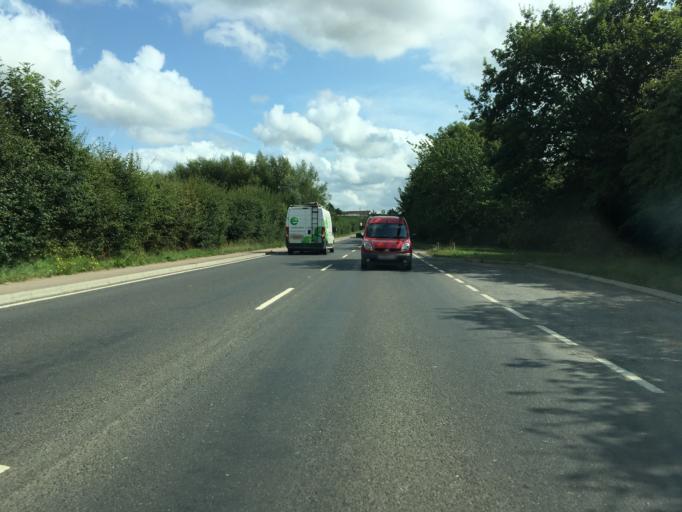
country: GB
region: England
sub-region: Kent
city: Headcorn
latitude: 51.2032
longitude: 0.5930
